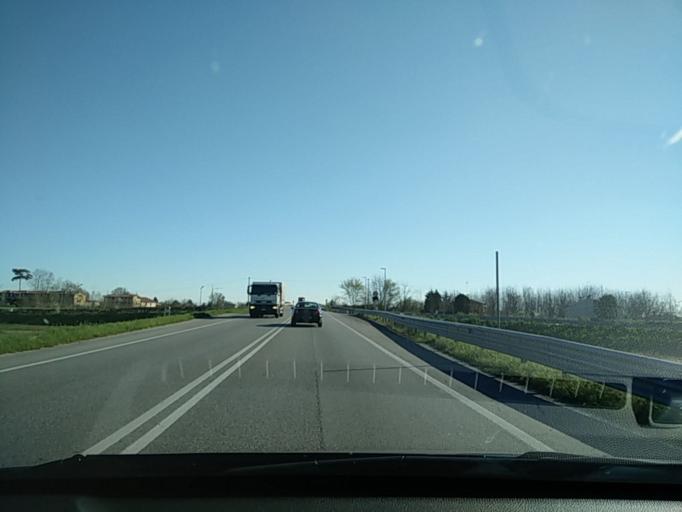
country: IT
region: Veneto
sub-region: Provincia di Treviso
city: Oderzo
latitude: 45.7915
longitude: 12.4887
